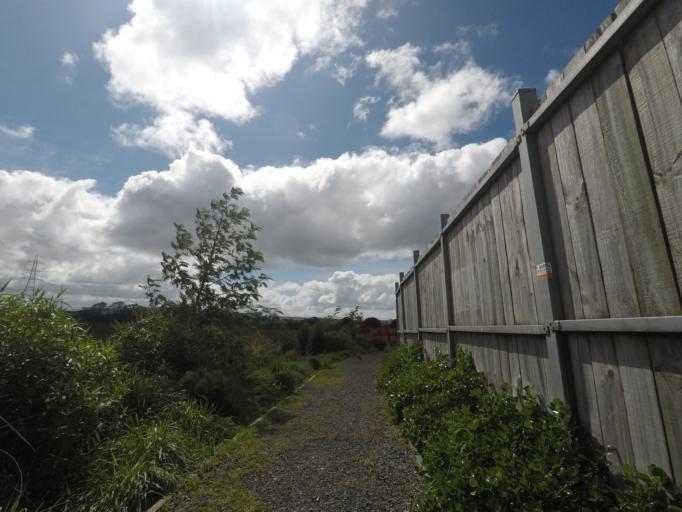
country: NZ
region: Auckland
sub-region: Auckland
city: Rosebank
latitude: -36.8775
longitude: 174.6656
